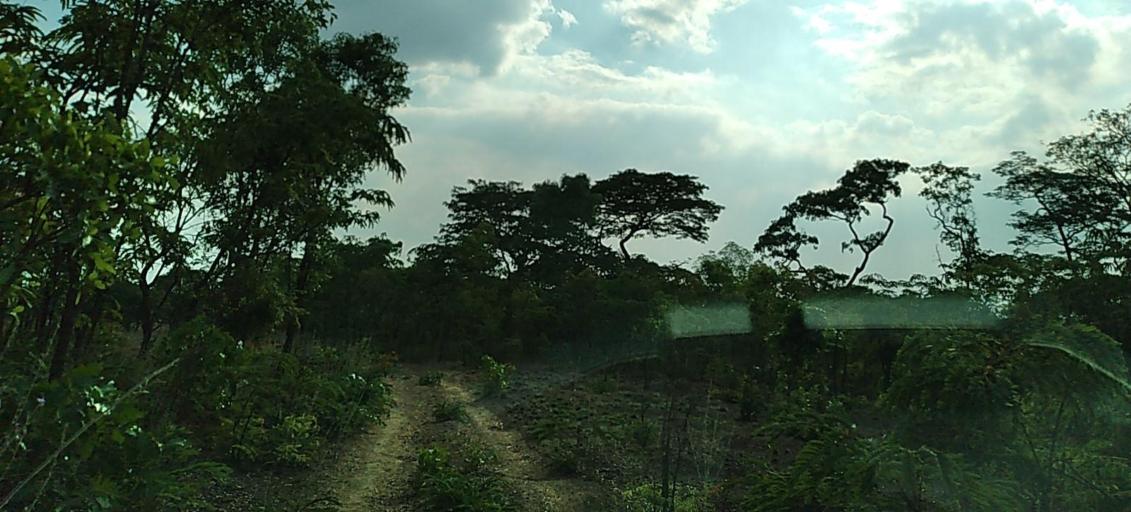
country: ZM
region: Copperbelt
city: Chililabombwe
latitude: -12.3590
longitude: 27.3942
